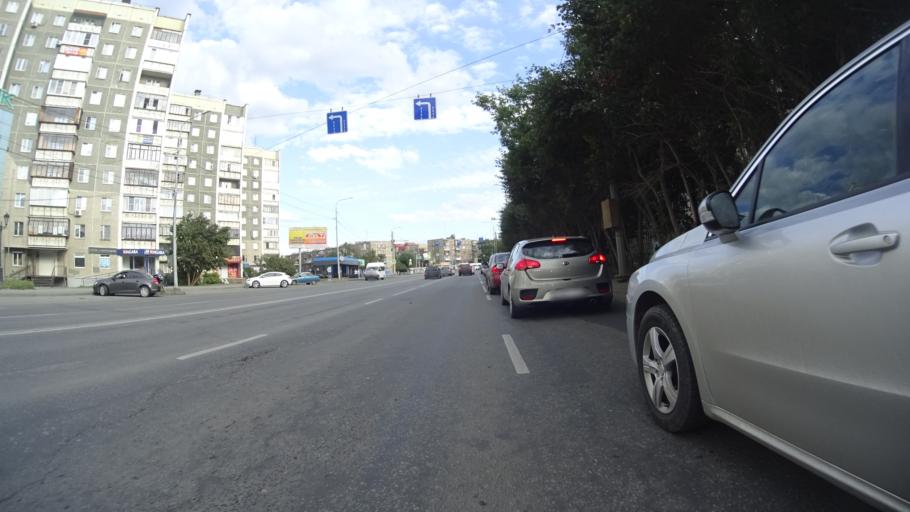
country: RU
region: Chelyabinsk
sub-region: Gorod Chelyabinsk
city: Chelyabinsk
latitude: 55.1993
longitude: 61.3307
